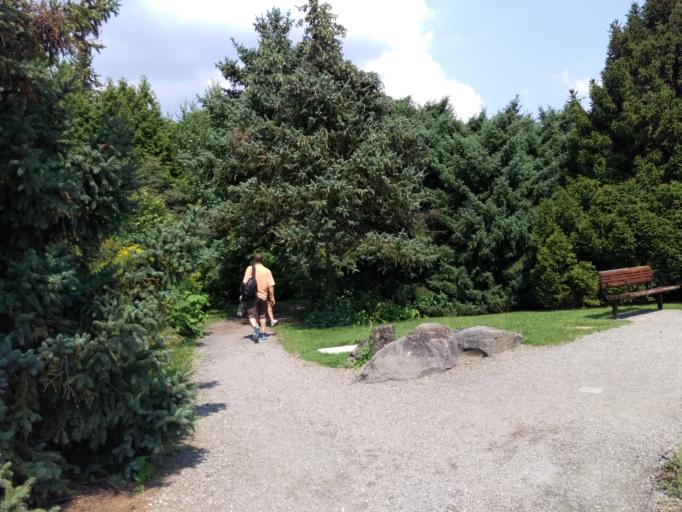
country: CA
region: Quebec
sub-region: Montreal
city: Saint-Leonard
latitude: 45.5587
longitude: -73.5600
